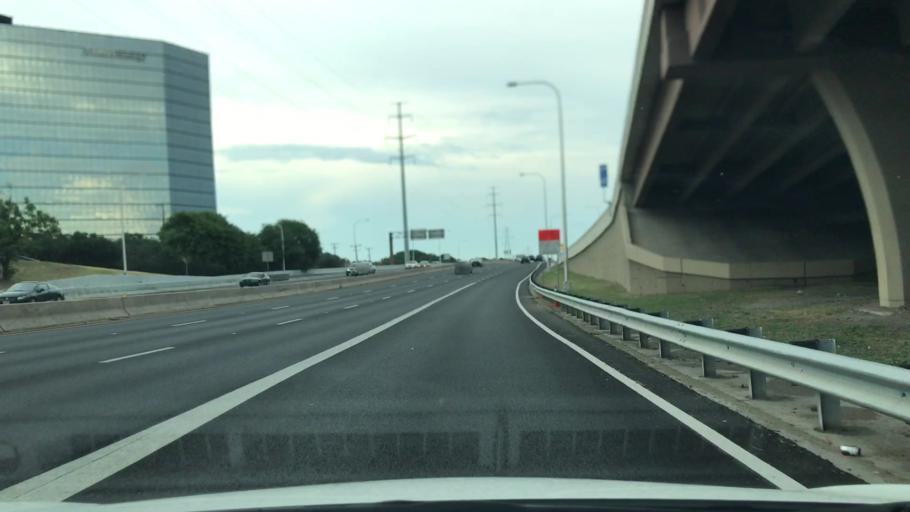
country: US
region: Texas
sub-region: Dallas County
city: Addison
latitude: 32.9238
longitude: -96.8198
